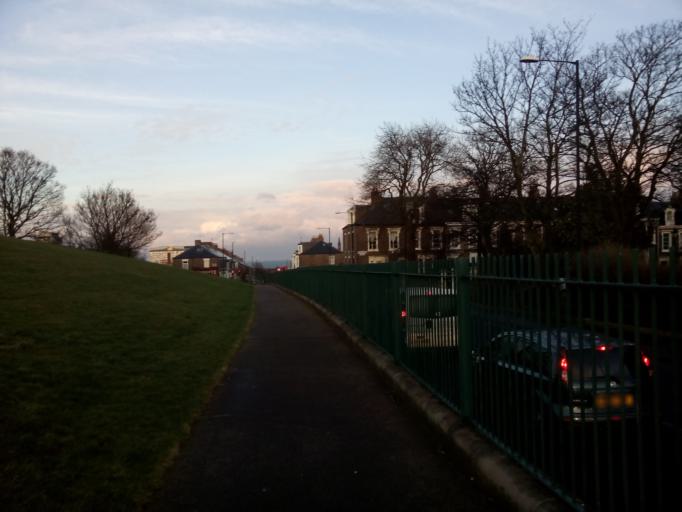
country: GB
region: England
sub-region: Sunderland
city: Sunderland
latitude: 54.9002
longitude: -1.3796
